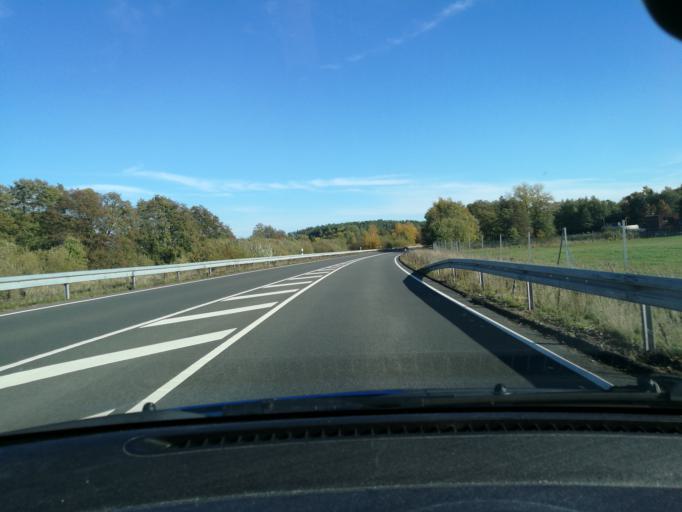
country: DE
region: Lower Saxony
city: Dahlenburg
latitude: 53.1962
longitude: 10.7230
